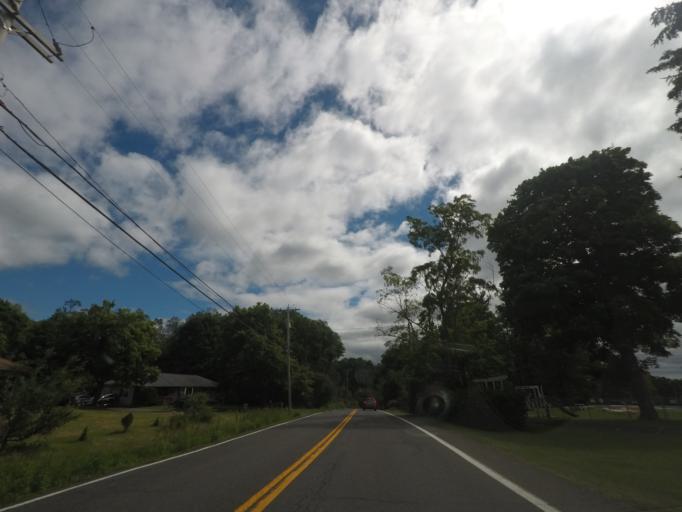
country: US
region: New York
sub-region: Columbia County
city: Philmont
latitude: 42.2348
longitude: -73.6953
